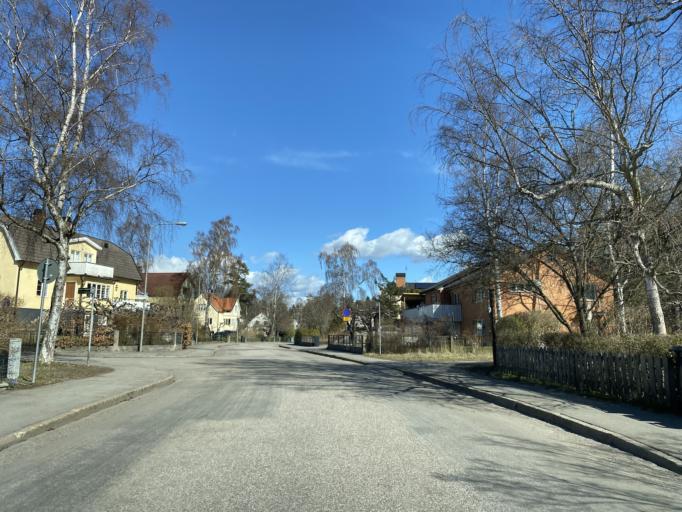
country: SE
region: Stockholm
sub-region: Stockholms Kommun
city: Arsta
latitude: 59.2737
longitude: 18.0607
